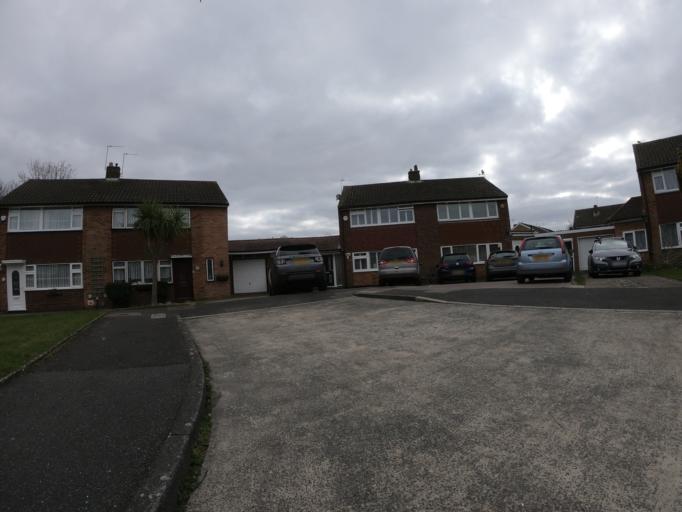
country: GB
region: England
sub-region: Greater London
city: Belvedere
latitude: 51.4862
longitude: 0.1515
